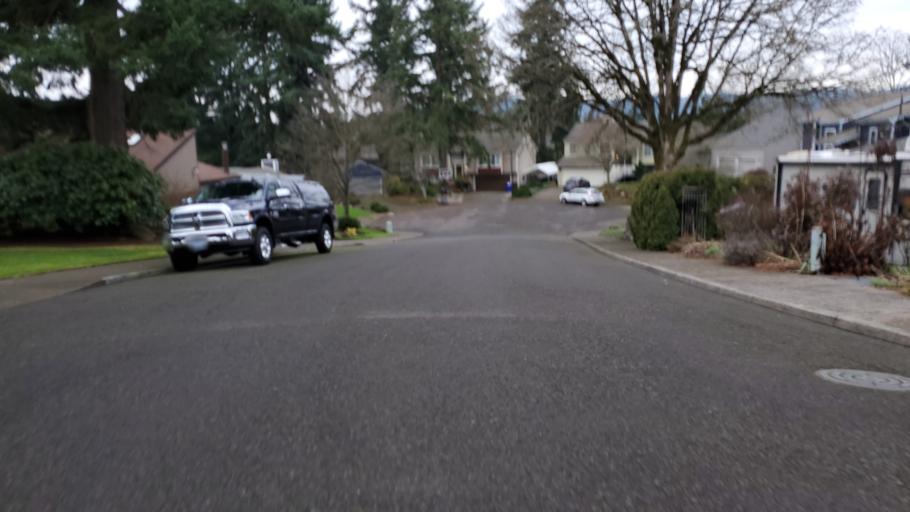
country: US
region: Oregon
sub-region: Clackamas County
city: Gladstone
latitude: 45.3898
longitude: -122.5950
